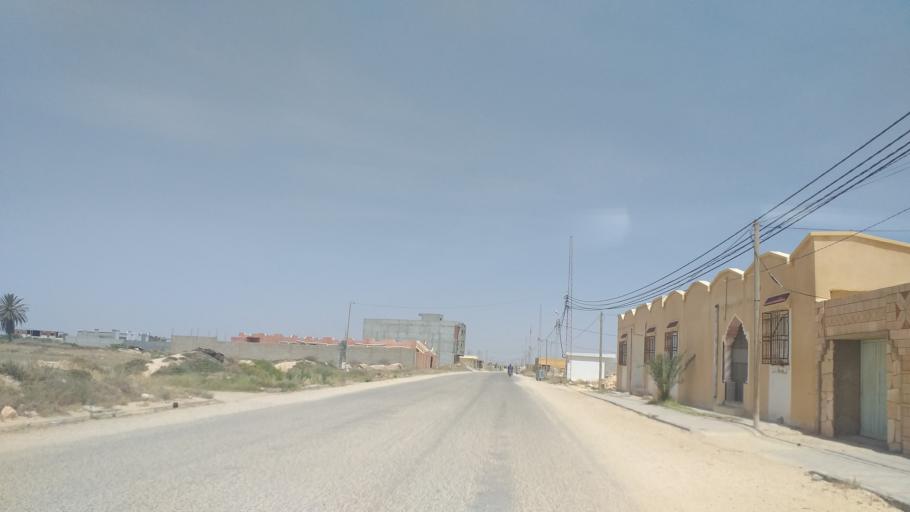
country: TN
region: Qabis
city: Gabes
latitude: 33.9528
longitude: 10.0674
